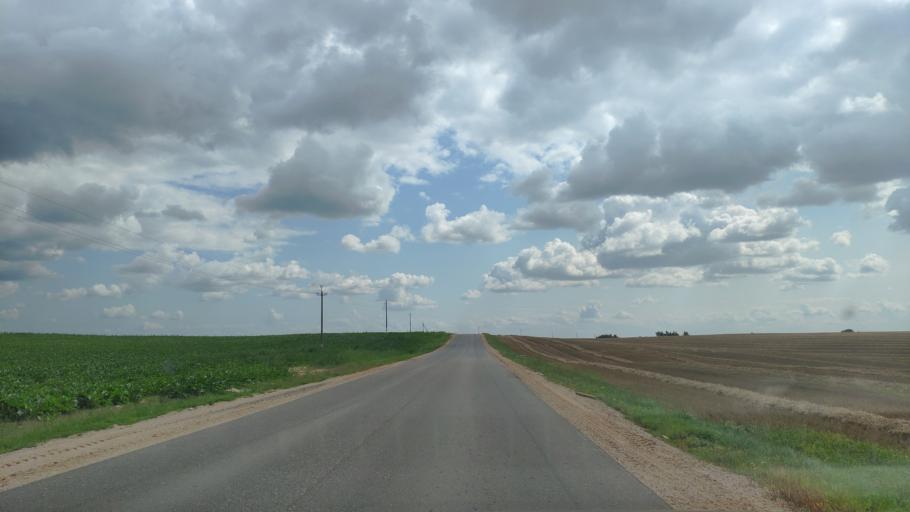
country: BY
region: Minsk
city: Khatsyezhyna
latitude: 53.8485
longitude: 27.3118
